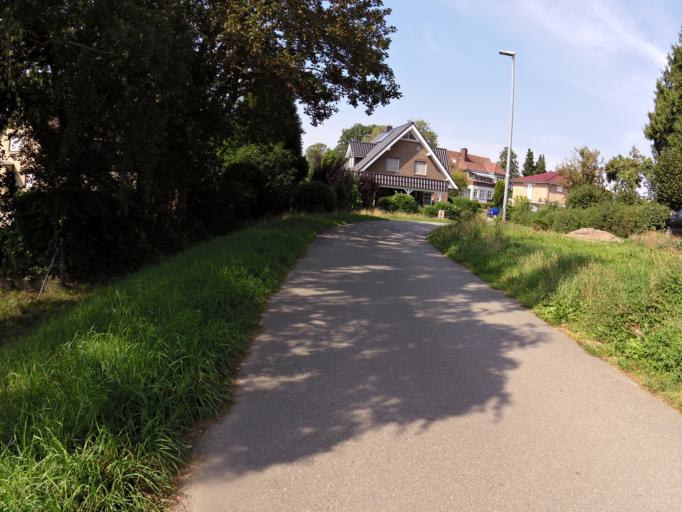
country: DE
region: Lower Saxony
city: Riede
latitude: 53.0141
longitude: 8.8869
